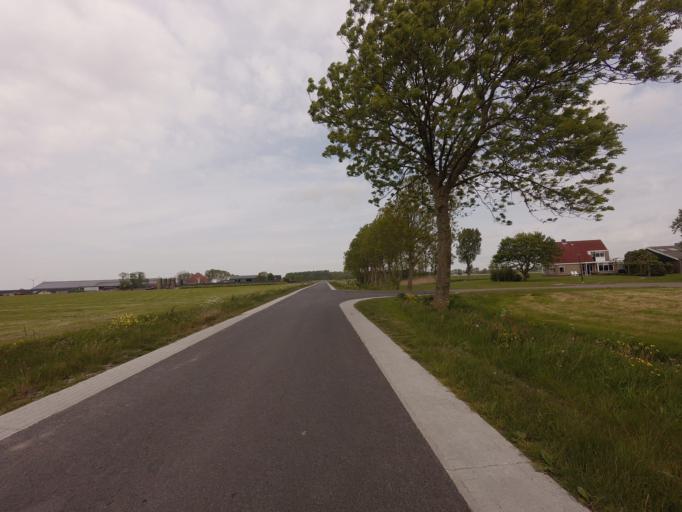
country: NL
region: Friesland
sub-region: Sudwest Fryslan
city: Bolsward
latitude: 53.0883
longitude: 5.4828
